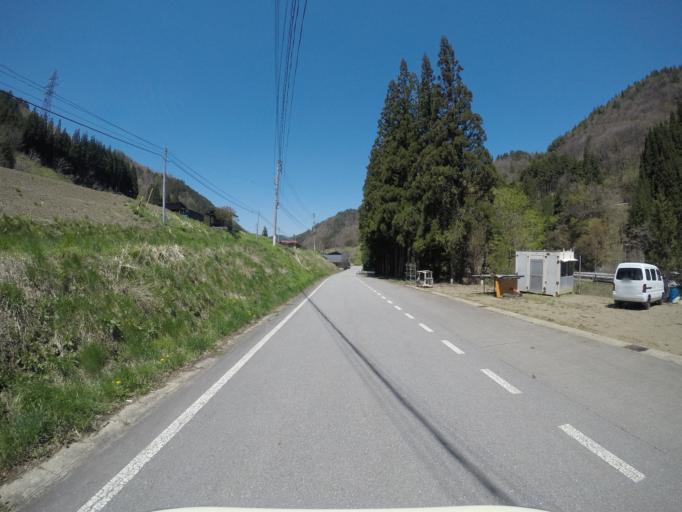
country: JP
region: Gifu
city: Takayama
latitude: 36.1704
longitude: 137.4316
